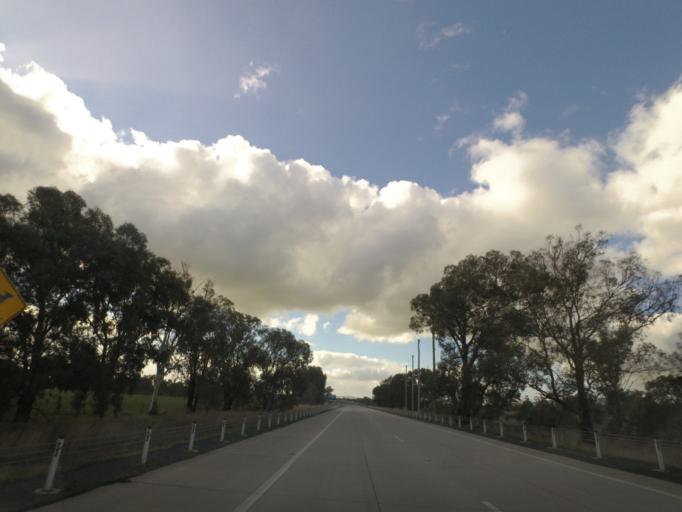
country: AU
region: New South Wales
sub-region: Greater Hume Shire
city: Holbrook
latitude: -35.7416
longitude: 147.3022
